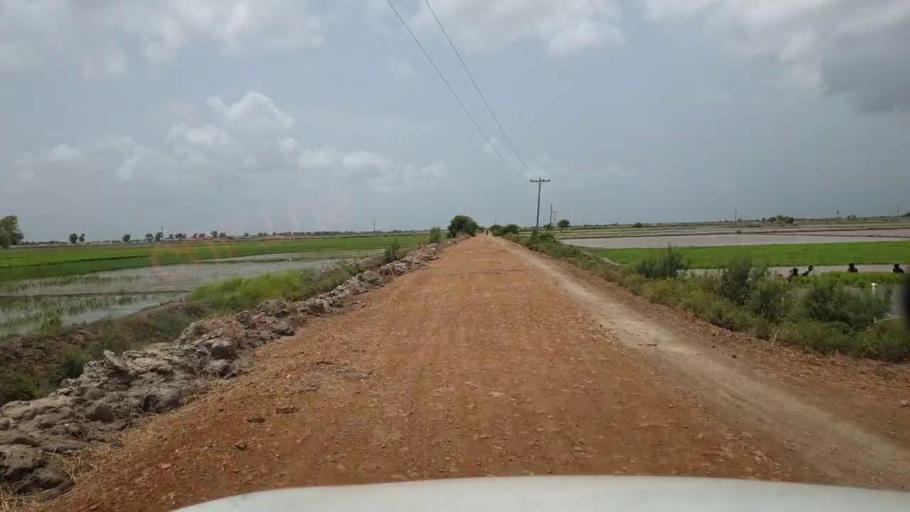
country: PK
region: Sindh
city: Kario
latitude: 24.7610
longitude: 68.4577
